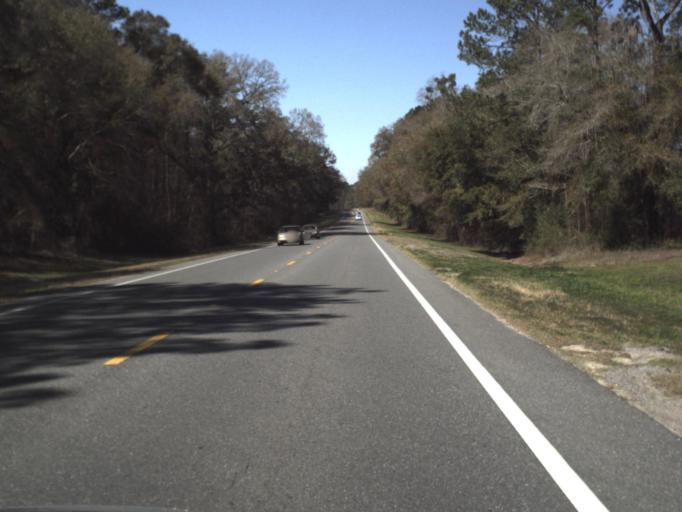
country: US
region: Florida
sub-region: Jackson County
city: Marianna
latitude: 30.7385
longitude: -85.1163
